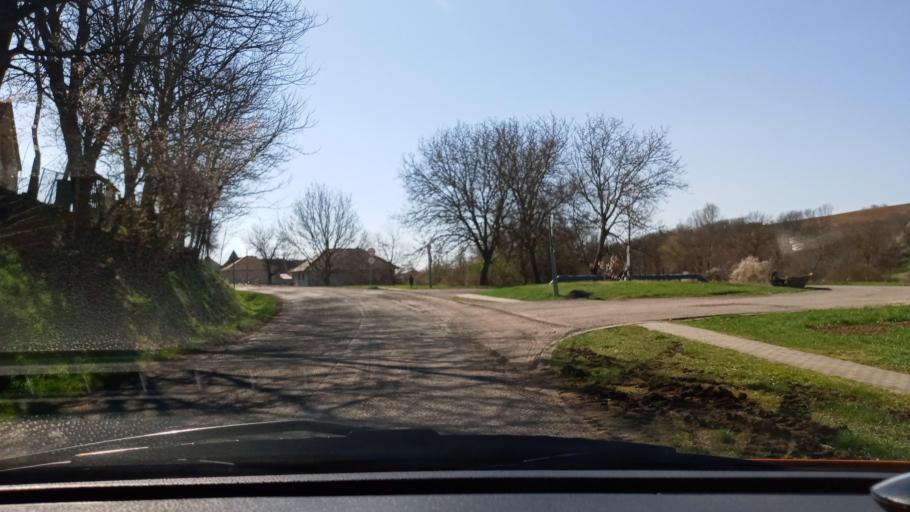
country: HU
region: Baranya
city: Kozarmisleny
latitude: 46.0180
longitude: 18.4086
